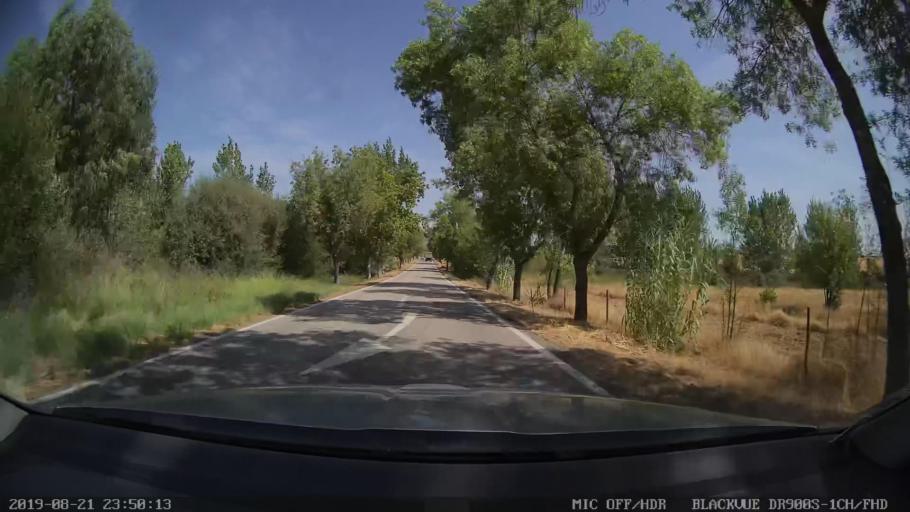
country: PT
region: Castelo Branco
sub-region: Idanha-A-Nova
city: Idanha-a-Nova
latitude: 39.8869
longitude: -7.2437
